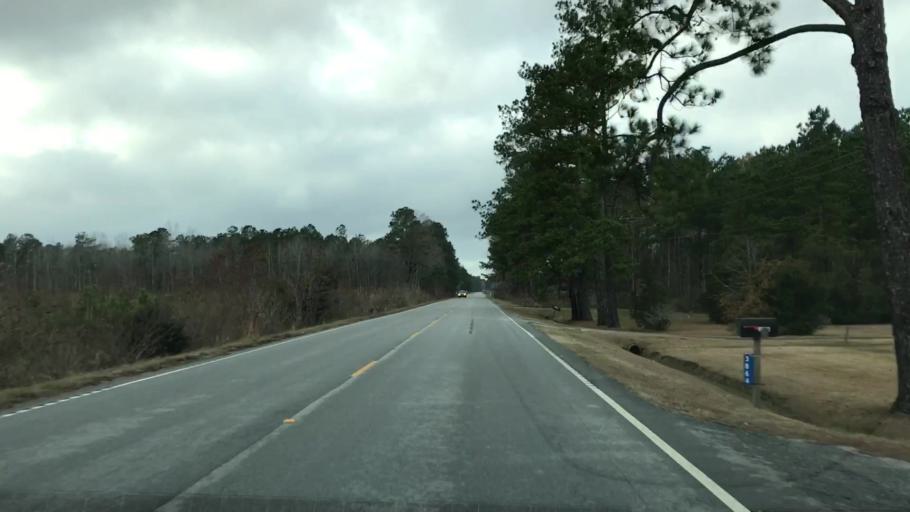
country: US
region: South Carolina
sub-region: Berkeley County
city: Saint Stephen
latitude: 33.2832
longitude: -79.7400
